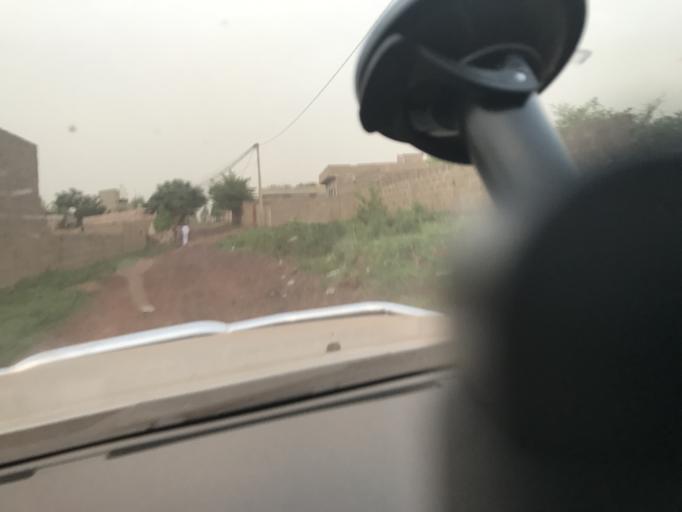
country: ML
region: Bamako
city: Bamako
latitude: 12.6493
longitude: -7.8801
